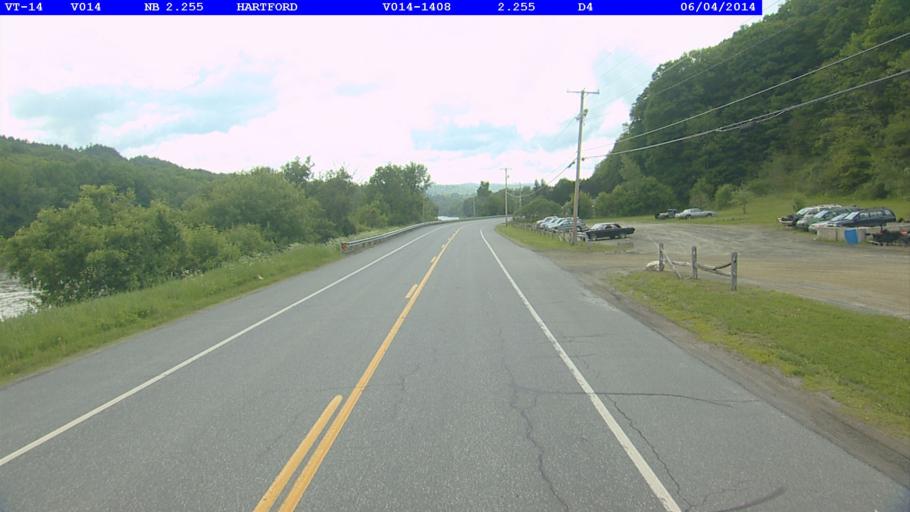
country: US
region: Vermont
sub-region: Windsor County
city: White River Junction
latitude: 43.6669
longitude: -72.3585
